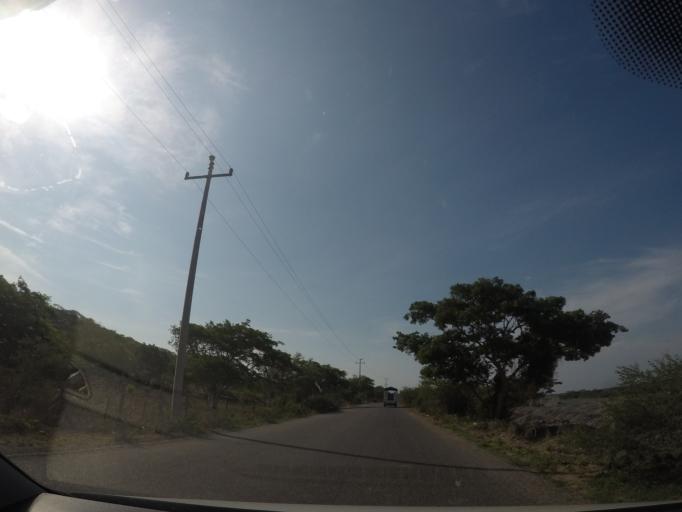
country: MX
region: Oaxaca
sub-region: Salina Cruz
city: Salina Cruz
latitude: 16.2343
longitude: -95.1512
